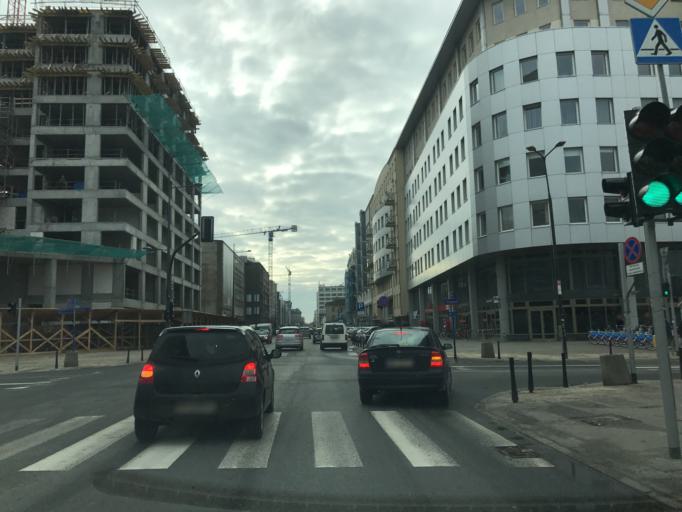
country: PL
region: Masovian Voivodeship
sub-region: Warszawa
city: Wola
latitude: 52.2350
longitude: 20.9905
